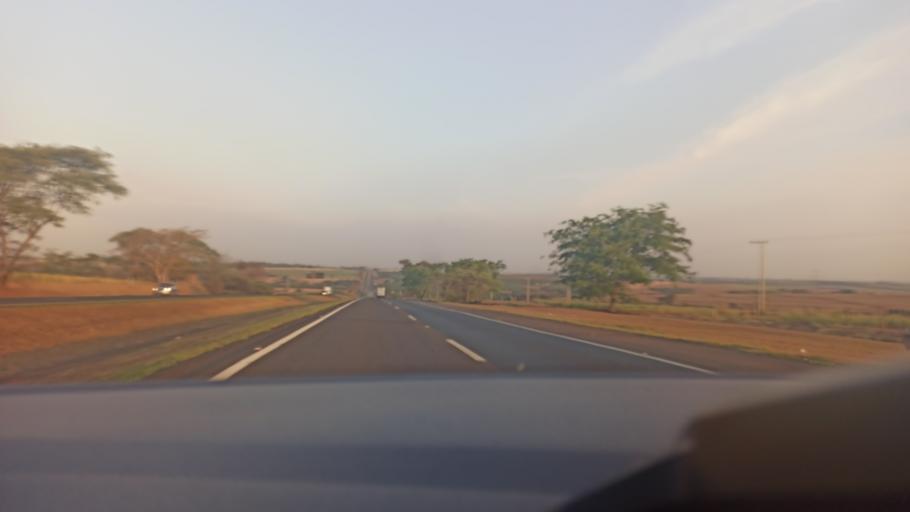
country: BR
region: Sao Paulo
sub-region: Santa Adelia
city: Santa Adelia
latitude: -21.3874
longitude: -48.7260
